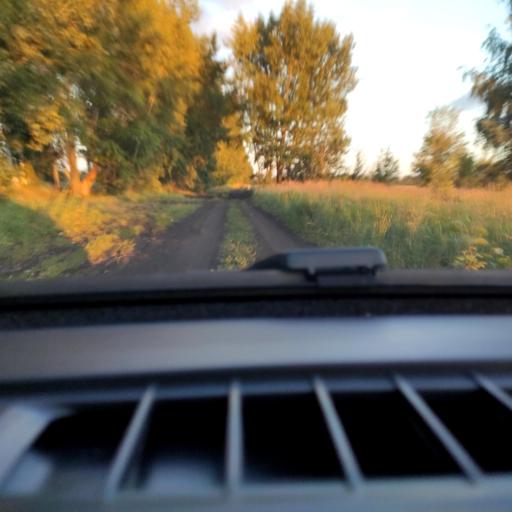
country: RU
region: Voronezj
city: Panino
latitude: 51.5712
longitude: 39.8819
